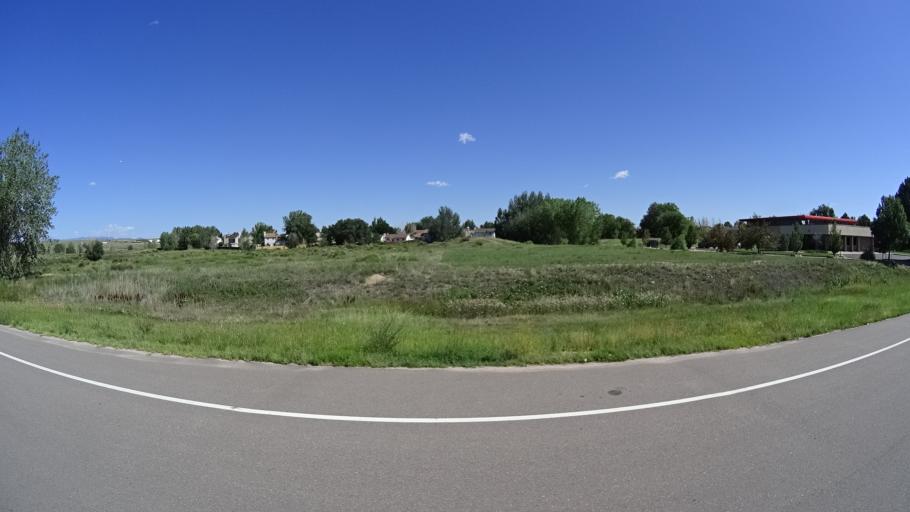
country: US
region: Colorado
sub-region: El Paso County
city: Security-Widefield
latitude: 38.7622
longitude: -104.6561
